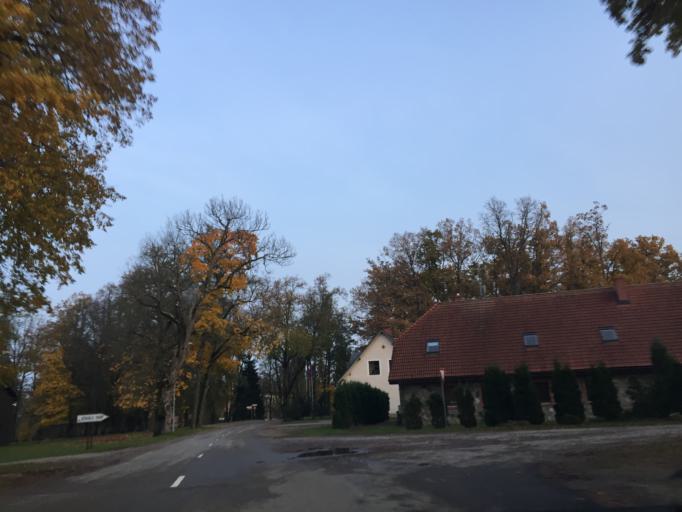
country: LV
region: Cesu Rajons
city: Cesis
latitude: 57.3130
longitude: 25.1565
